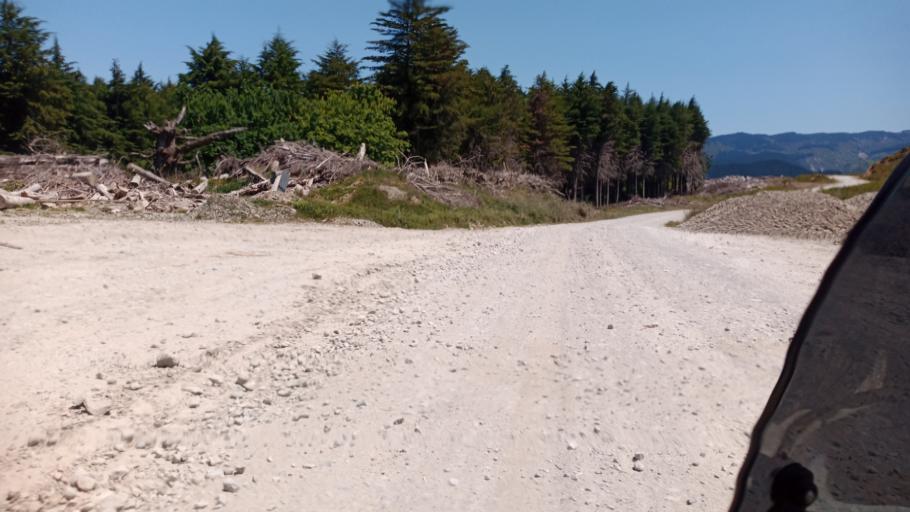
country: NZ
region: Gisborne
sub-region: Gisborne District
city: Gisborne
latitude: -38.2923
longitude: 178.0193
